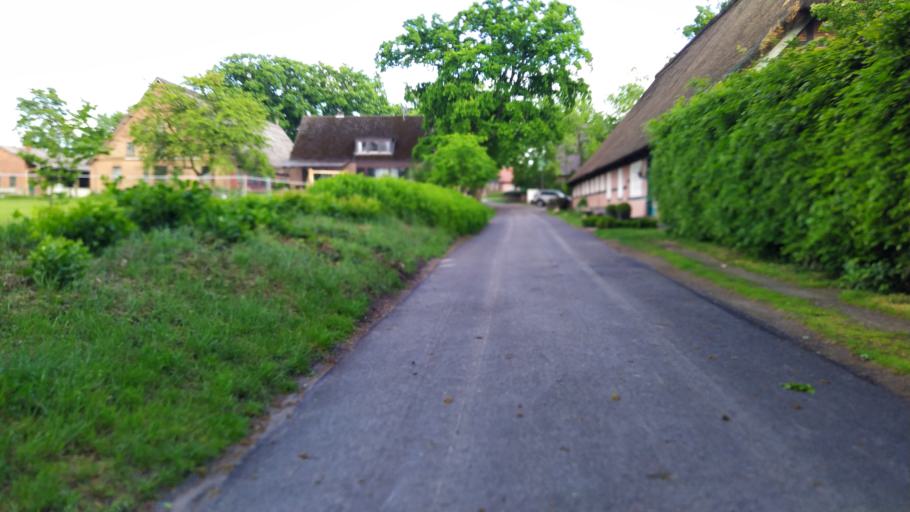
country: DE
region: Lower Saxony
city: Farven
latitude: 53.4360
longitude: 9.3214
